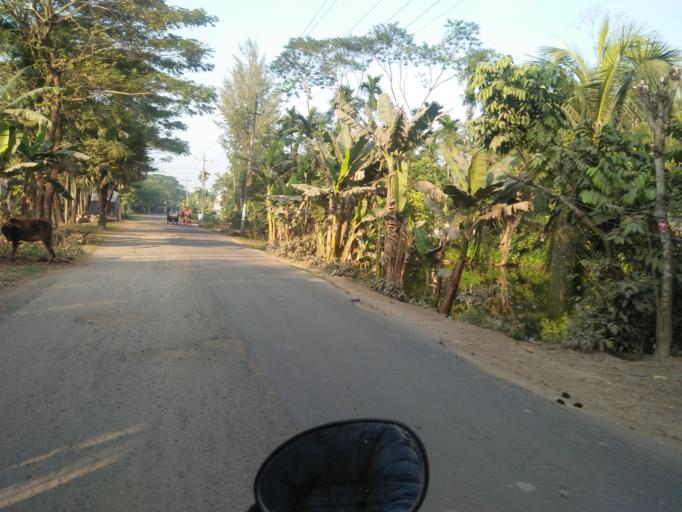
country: BD
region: Barisal
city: Bhola
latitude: 22.7476
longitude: 90.6344
